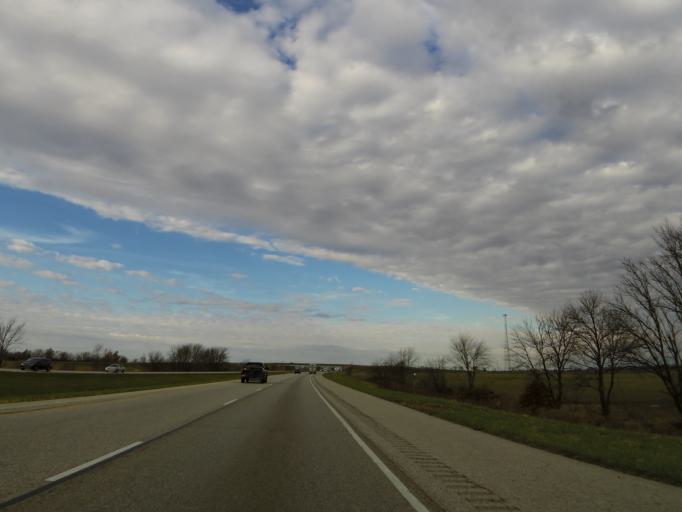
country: US
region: Illinois
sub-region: Washington County
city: Nashville
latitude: 38.4120
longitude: -89.4308
